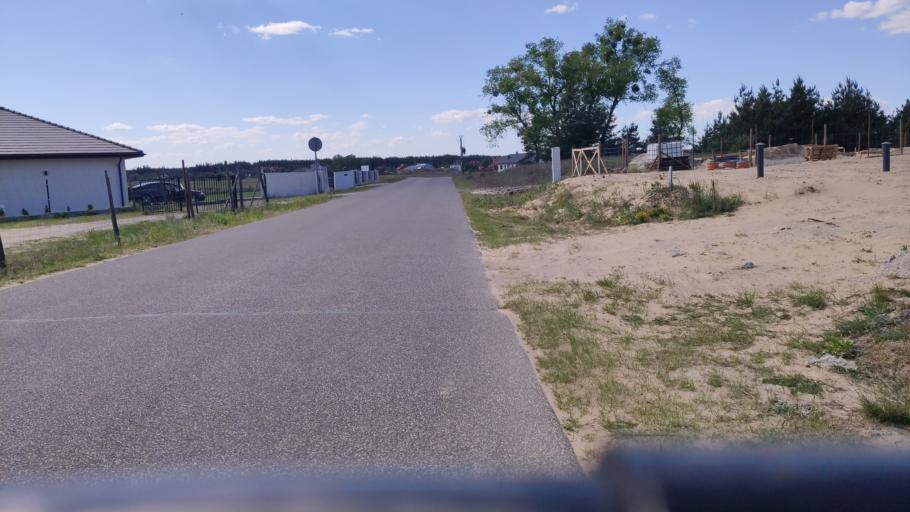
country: PL
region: Kujawsko-Pomorskie
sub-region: Wloclawek
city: Wloclawek
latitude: 52.5848
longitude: 19.0925
